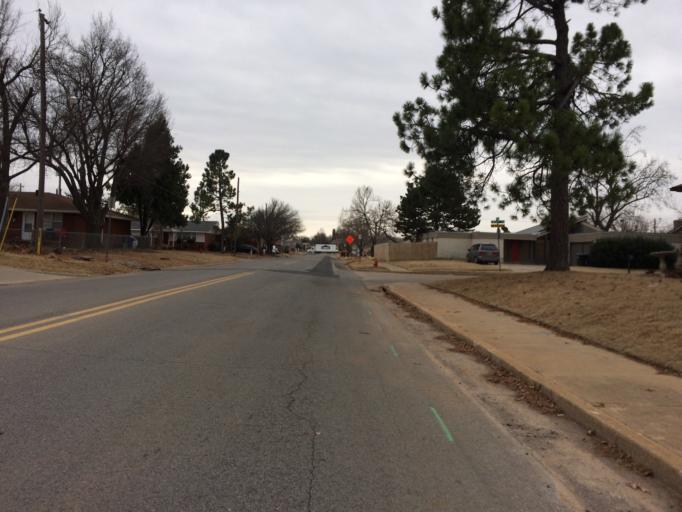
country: US
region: Oklahoma
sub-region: Cleveland County
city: Norman
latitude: 35.2058
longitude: -97.4635
